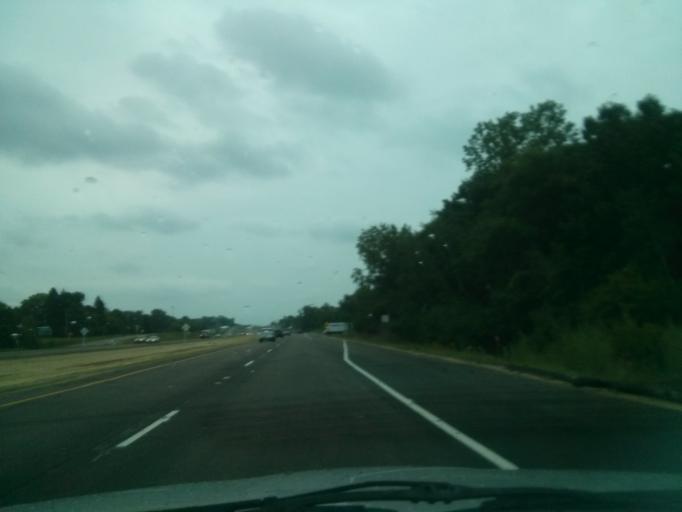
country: US
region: Minnesota
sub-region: Washington County
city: Mahtomedi
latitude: 45.0355
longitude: -92.9411
